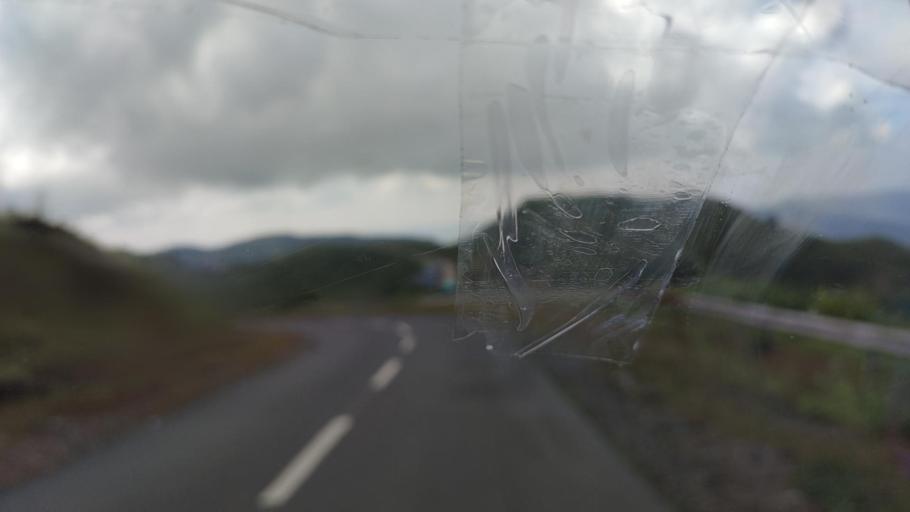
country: MM
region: Magway
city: Minbu
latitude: 19.8355
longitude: 94.2897
